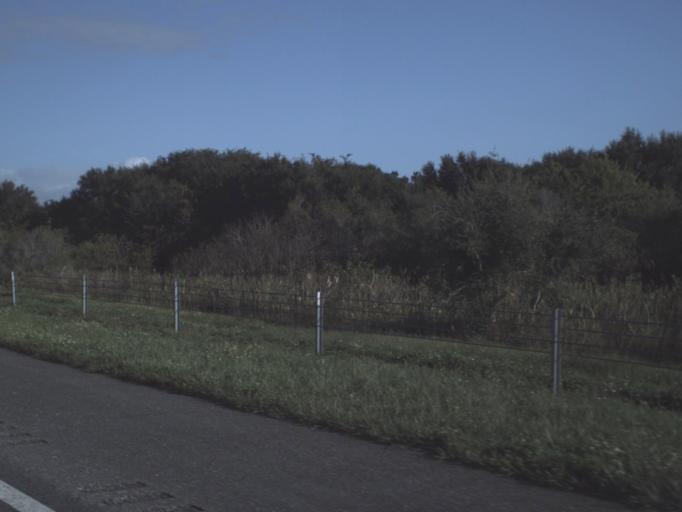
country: US
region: Florida
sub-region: Indian River County
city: Fellsmere
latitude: 27.8057
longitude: -80.9977
